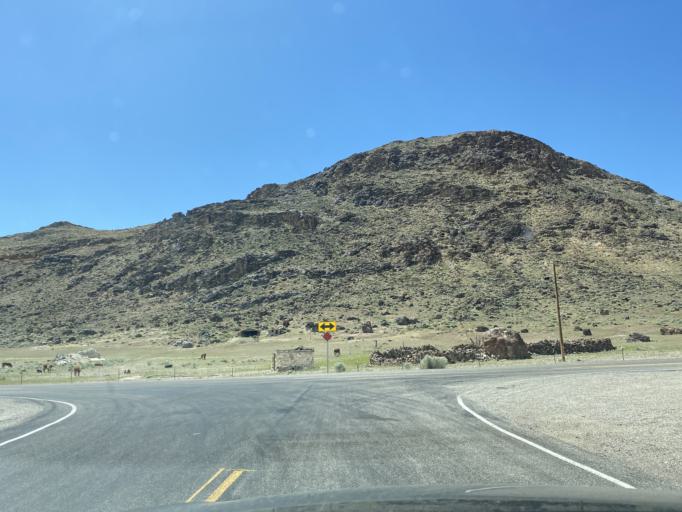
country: US
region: Nevada
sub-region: Nye County
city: Tonopah
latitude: 38.1910
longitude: -116.3696
